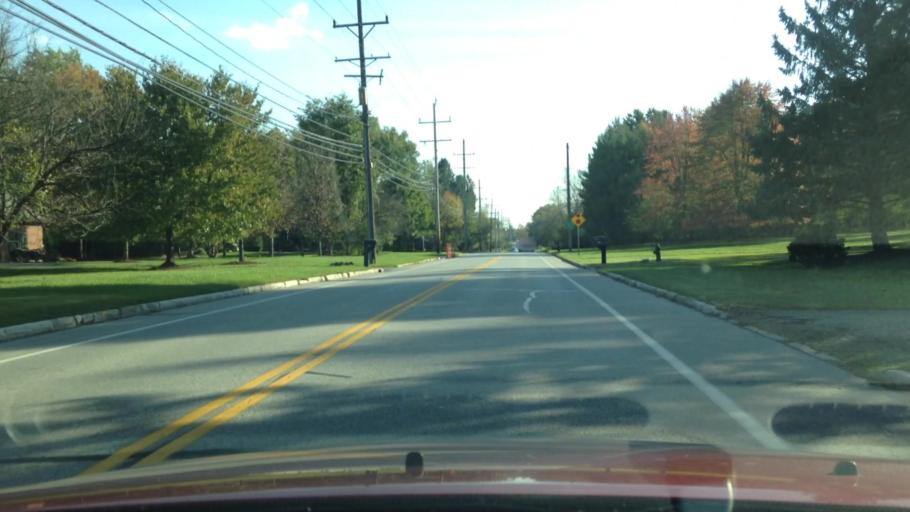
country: US
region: Ohio
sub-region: Cuyahoga County
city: Pepper Pike
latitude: 41.4688
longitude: -81.4635
